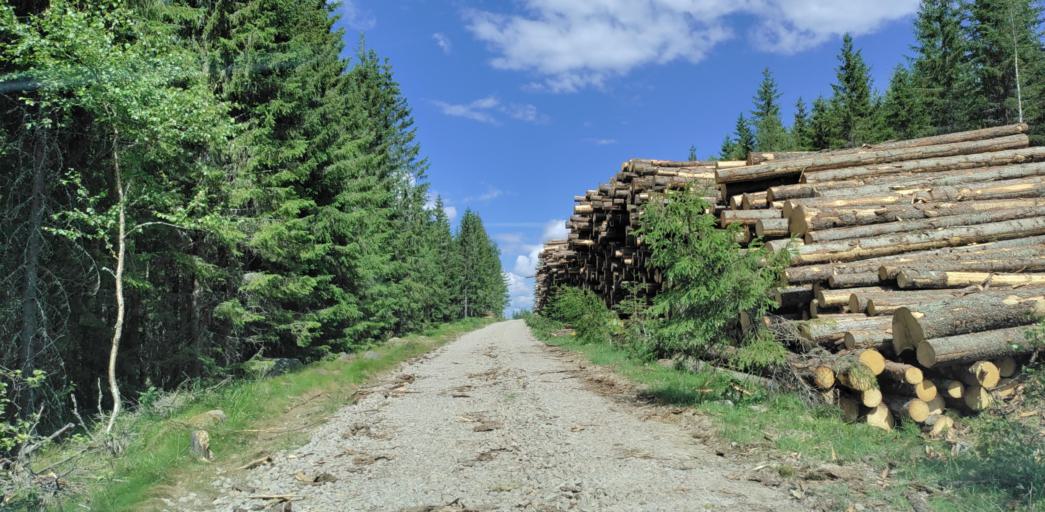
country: SE
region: Vaermland
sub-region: Hagfors Kommun
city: Ekshaerad
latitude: 60.0669
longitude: 13.3414
